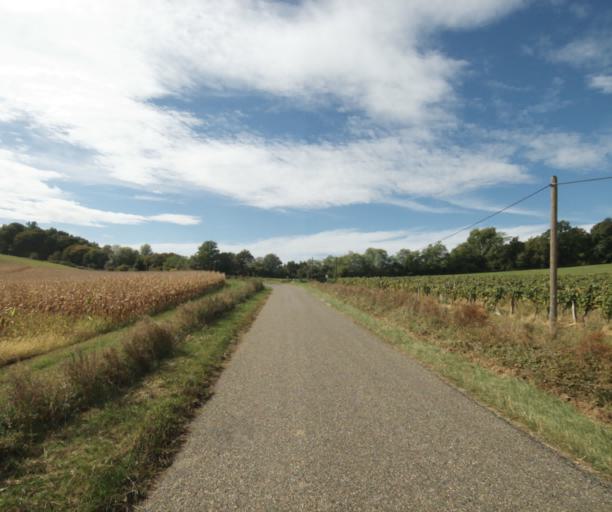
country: FR
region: Aquitaine
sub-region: Departement des Landes
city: Villeneuve-de-Marsan
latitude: 43.9004
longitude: -0.2137
